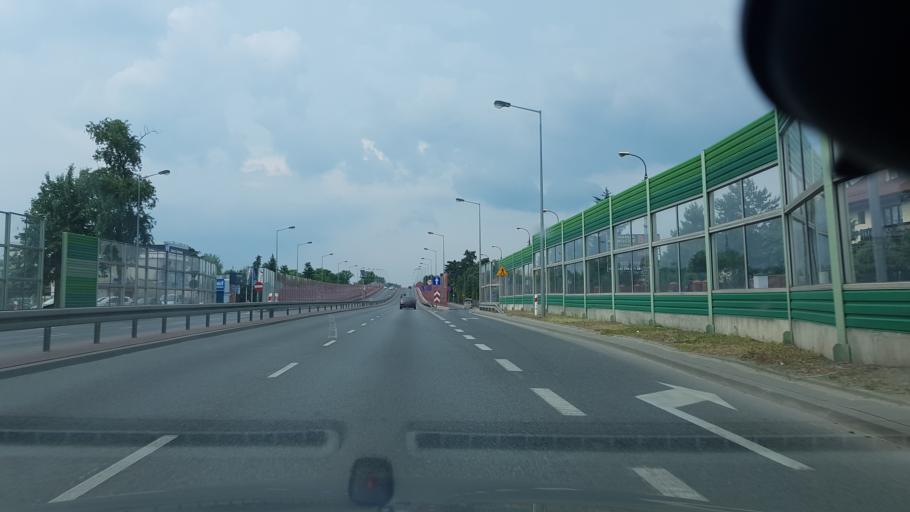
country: PL
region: Masovian Voivodeship
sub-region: Powiat legionowski
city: Legionowo
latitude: 52.3966
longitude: 20.9400
